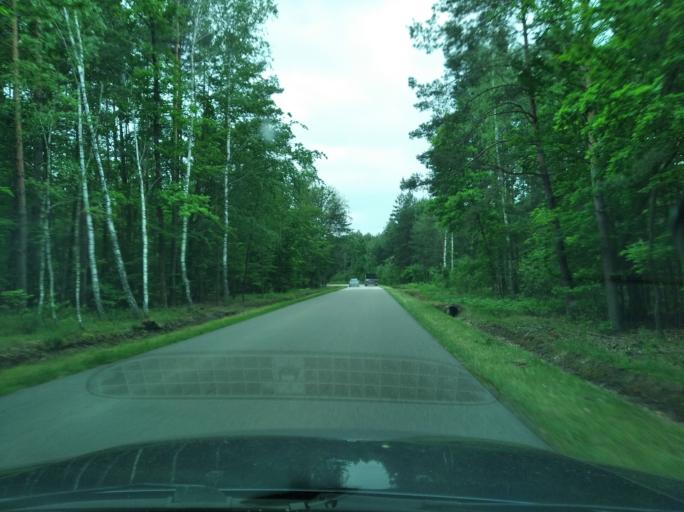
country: PL
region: Subcarpathian Voivodeship
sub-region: Powiat kolbuszowski
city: Niwiska
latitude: 50.2038
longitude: 21.6472
